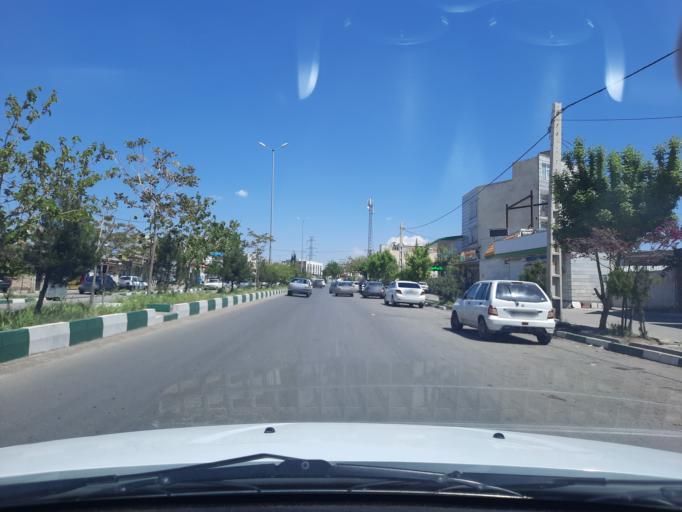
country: IR
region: Qazvin
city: Alvand
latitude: 36.2762
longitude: 50.1234
